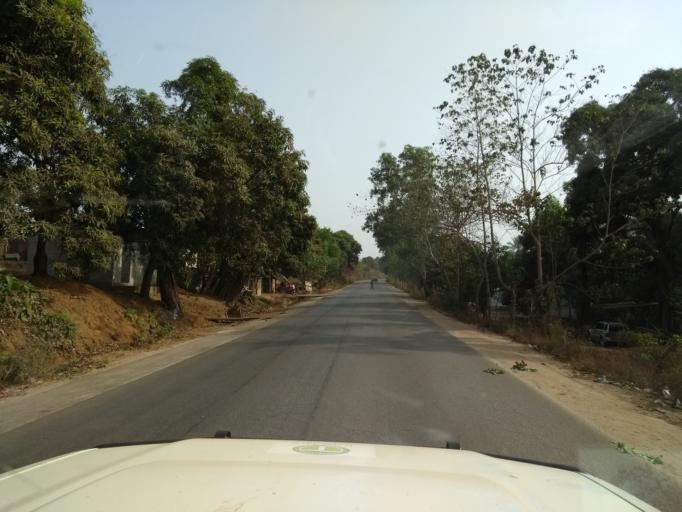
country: GN
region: Kindia
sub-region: Prefecture de Dubreka
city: Dubreka
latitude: 9.8434
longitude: -13.4873
